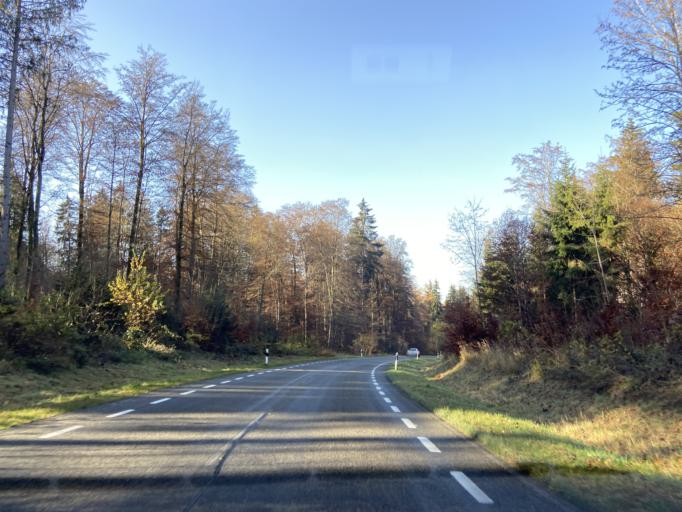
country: DE
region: Baden-Wuerttemberg
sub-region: Tuebingen Region
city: Sigmaringendorf
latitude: 48.0561
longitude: 9.2621
